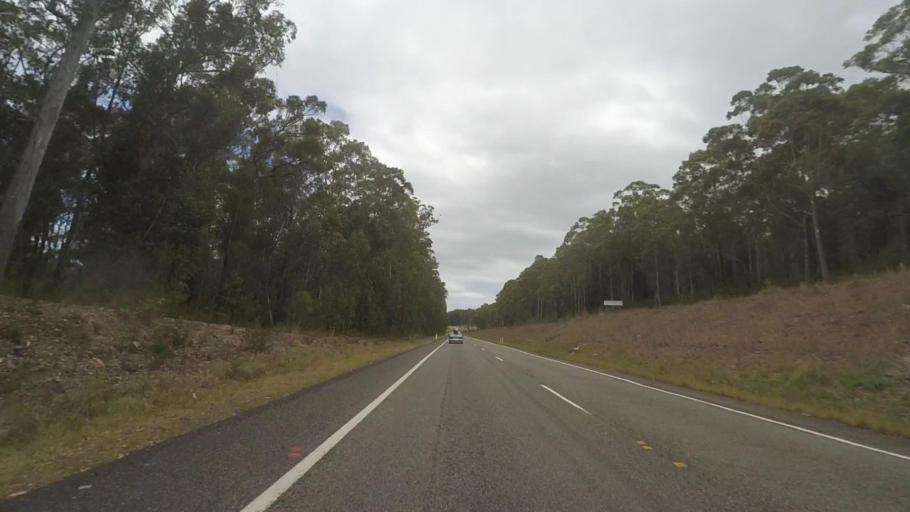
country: AU
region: New South Wales
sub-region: Shoalhaven Shire
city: Milton
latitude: -35.1301
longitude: 150.4687
